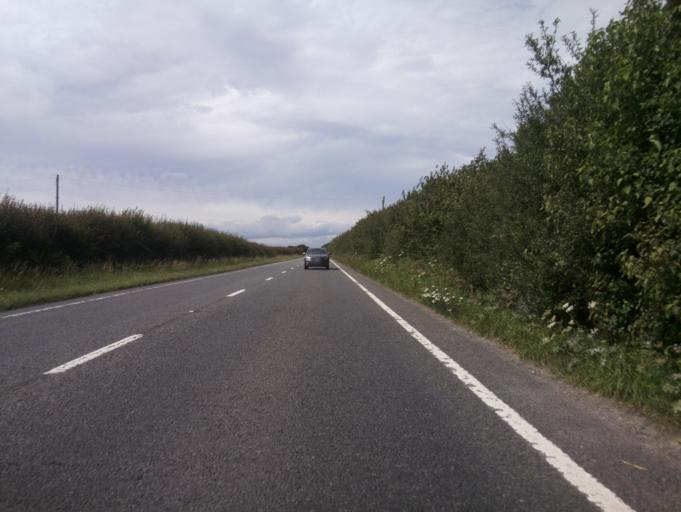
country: GB
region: England
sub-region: Dorset
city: Sherborne
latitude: 50.8086
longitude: -2.5531
